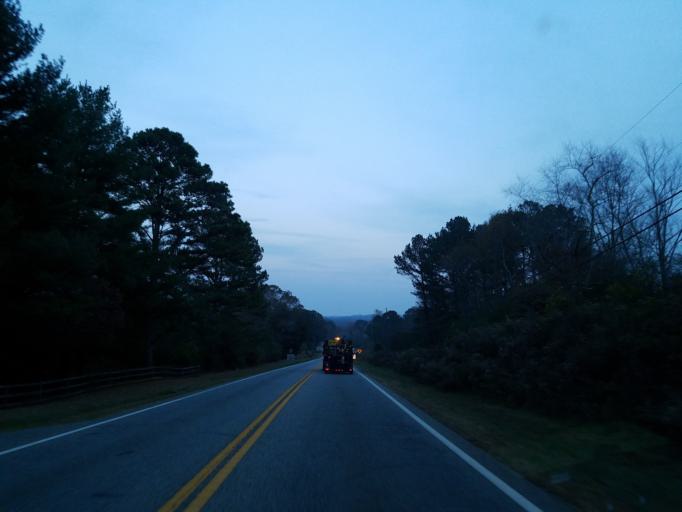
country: US
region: Georgia
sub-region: Pickens County
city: Jasper
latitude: 34.5116
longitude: -84.5614
